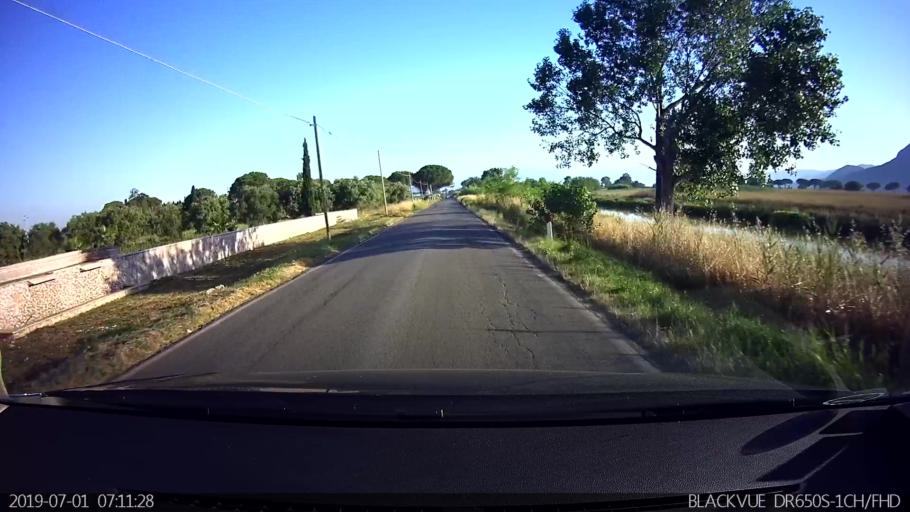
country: IT
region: Latium
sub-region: Provincia di Latina
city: Borgo Hermada
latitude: 41.3203
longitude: 13.1783
